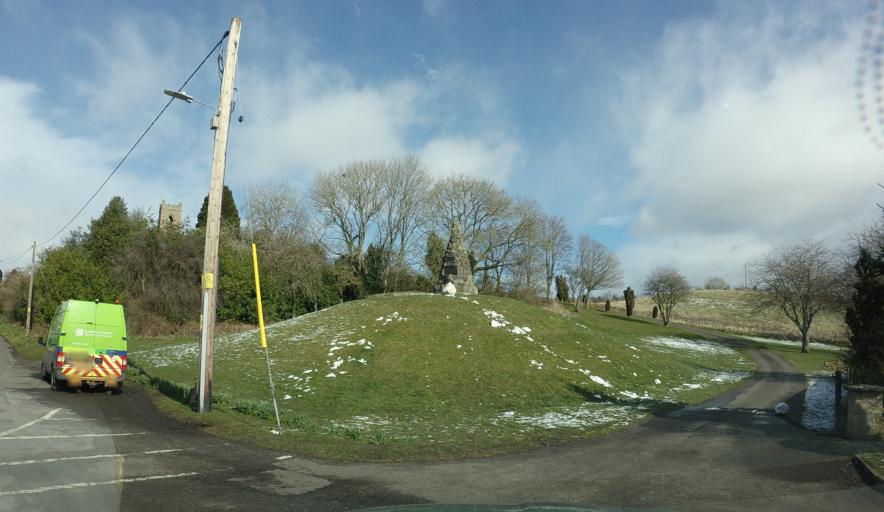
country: GB
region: Scotland
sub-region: Perth and Kinross
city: Bankfoot
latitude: 56.4993
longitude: -3.5130
